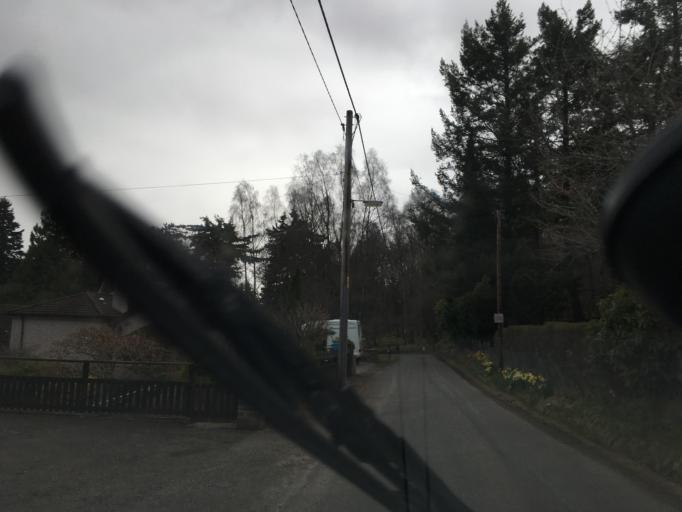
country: GB
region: Scotland
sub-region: Highland
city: Kingussie
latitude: 57.0819
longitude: -4.0567
